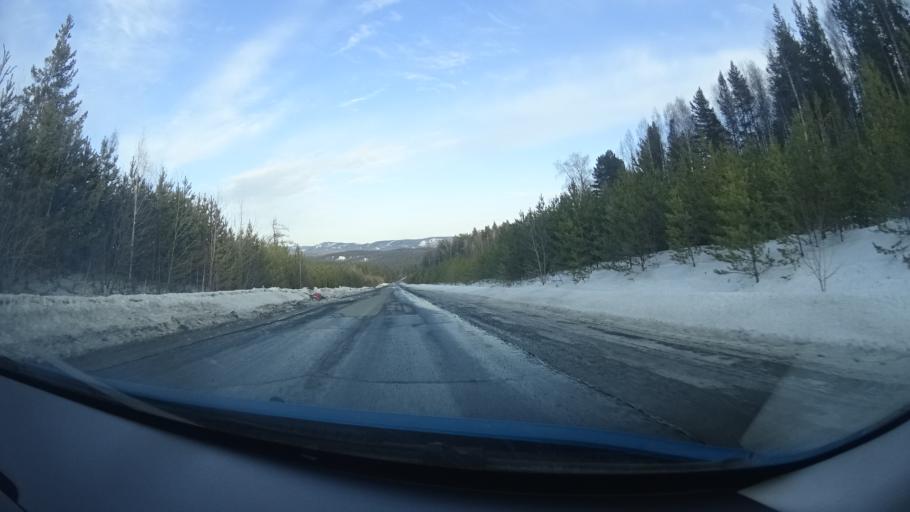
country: RU
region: Bashkortostan
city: Lomovka
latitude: 53.5235
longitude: 58.2727
